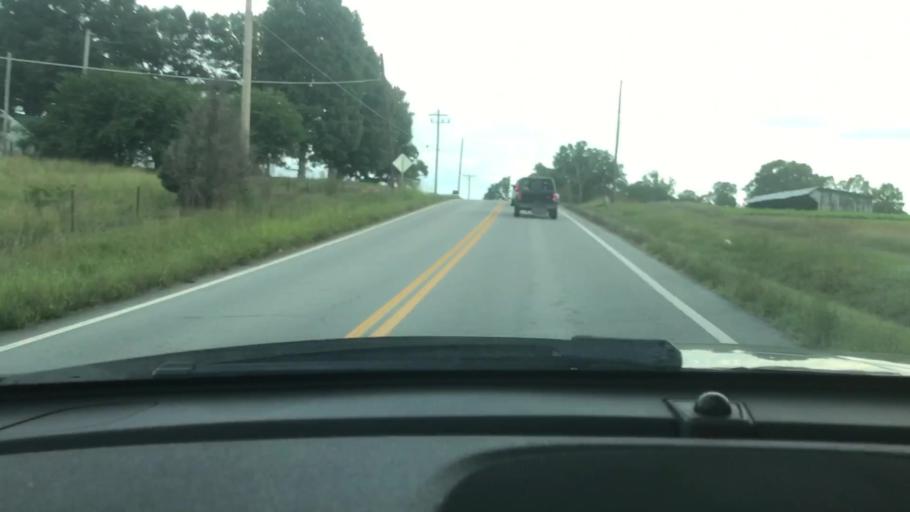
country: US
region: Tennessee
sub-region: Dickson County
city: Charlotte
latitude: 36.2280
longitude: -87.2543
